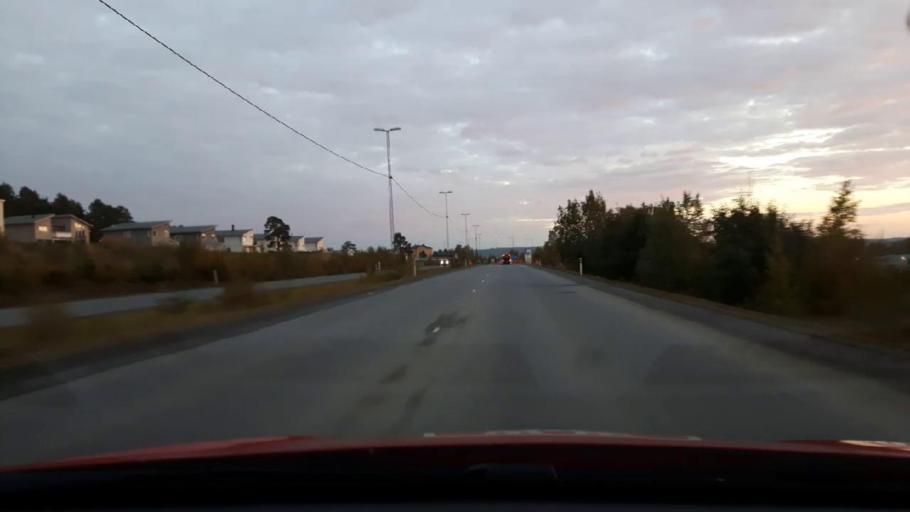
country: SE
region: Jaemtland
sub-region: OEstersunds Kommun
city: Ostersund
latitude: 63.1926
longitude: 14.6432
